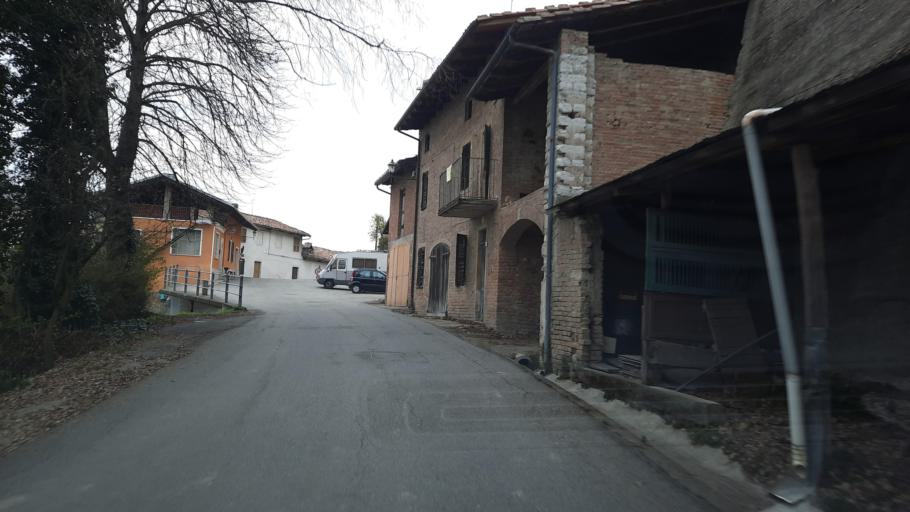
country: IT
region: Piedmont
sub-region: Provincia di Alessandria
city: Odalengo Grande
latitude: 45.1094
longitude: 8.1673
